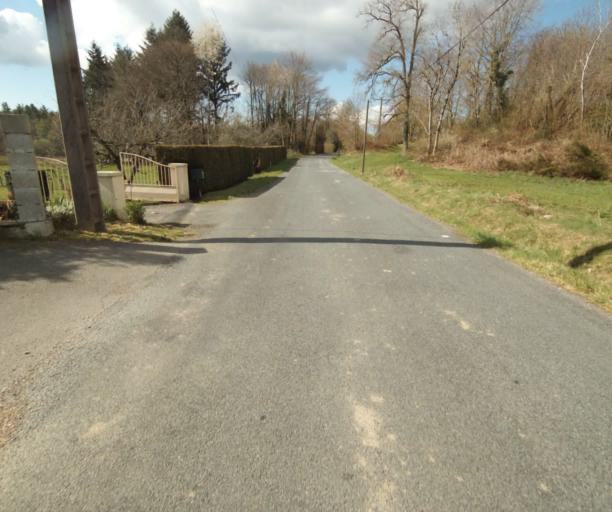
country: FR
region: Limousin
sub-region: Departement de la Correze
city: Argentat
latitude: 45.2235
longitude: 1.9313
